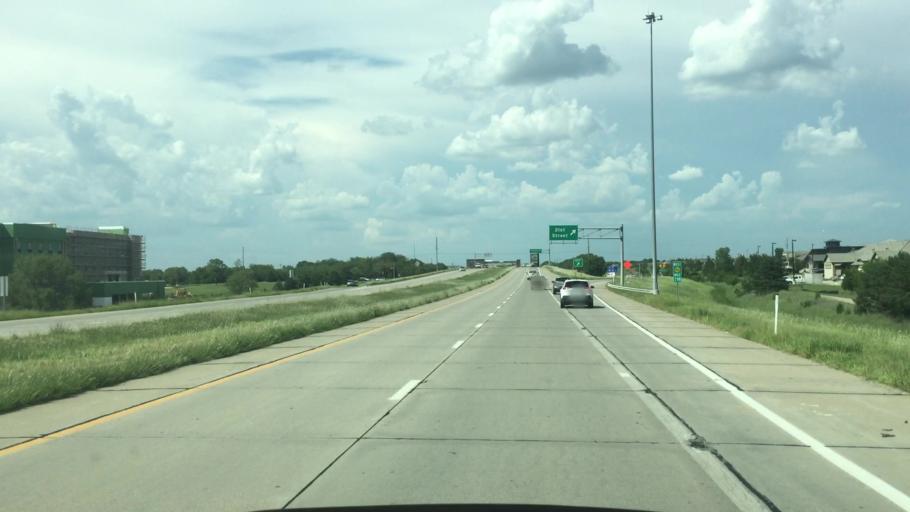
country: US
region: Kansas
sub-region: Butler County
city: Andover
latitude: 37.7192
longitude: -97.1994
